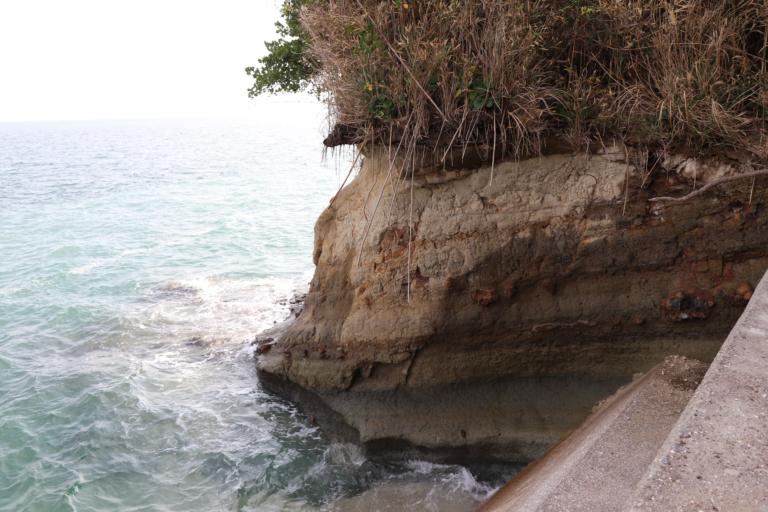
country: JP
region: Kumamoto
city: Hondo
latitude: 32.6288
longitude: 130.2554
